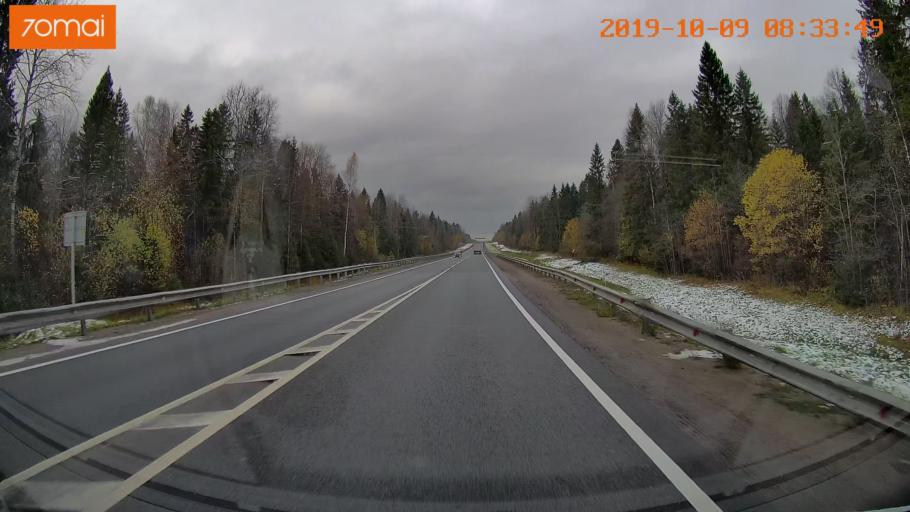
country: RU
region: Vologda
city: Gryazovets
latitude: 58.8876
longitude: 40.1899
